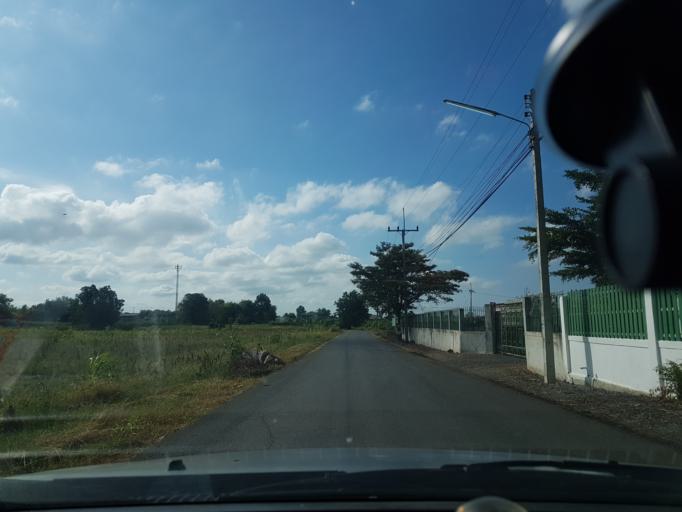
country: TH
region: Lop Buri
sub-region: Amphoe Tha Luang
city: Tha Luang
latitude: 15.0713
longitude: 101.0485
